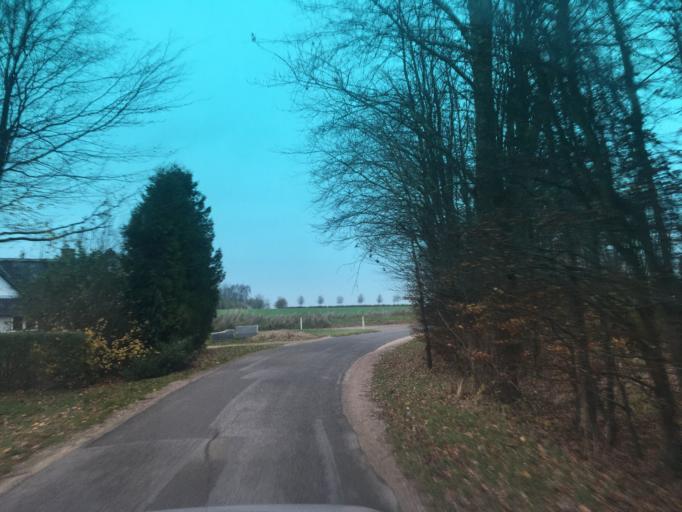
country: DK
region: Zealand
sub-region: Slagelse Kommune
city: Skaelskor
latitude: 55.2693
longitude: 11.4206
